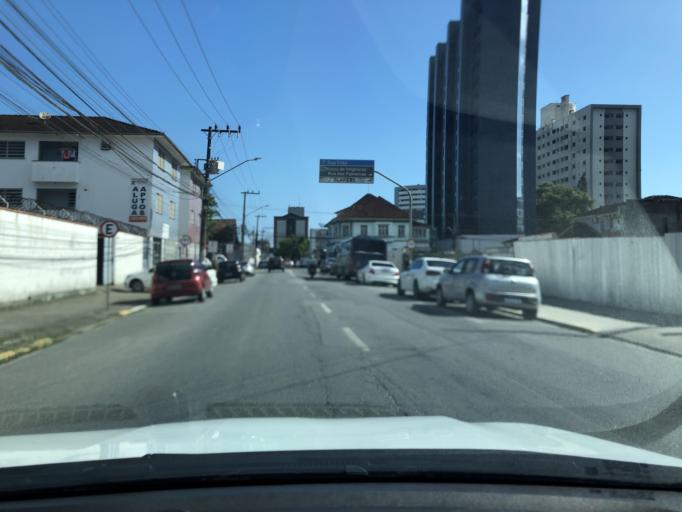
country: BR
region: Santa Catarina
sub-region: Joinville
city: Joinville
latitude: -26.3034
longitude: -48.8421
